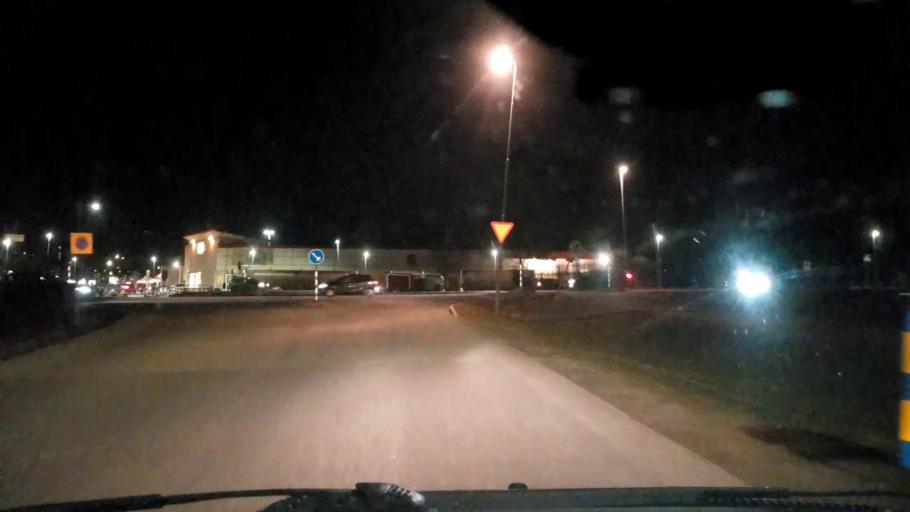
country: SE
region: Stockholm
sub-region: Haninge Kommun
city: Haninge
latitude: 59.1821
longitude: 18.1608
